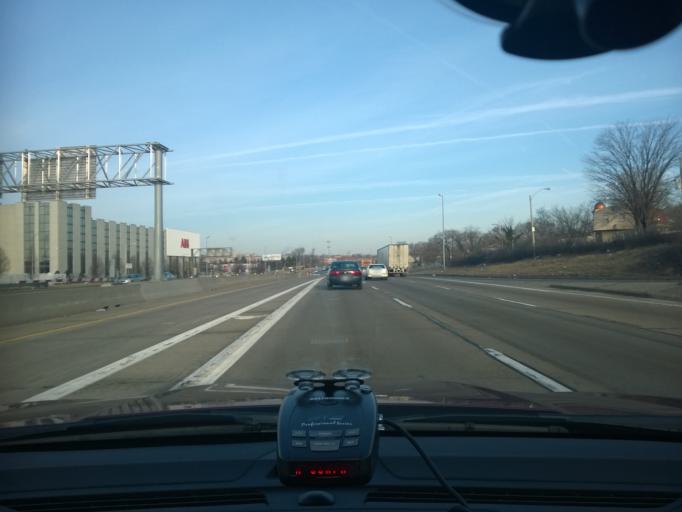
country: US
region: Missouri
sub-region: Saint Louis County
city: Pine Lawn
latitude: 38.6895
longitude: -90.2531
